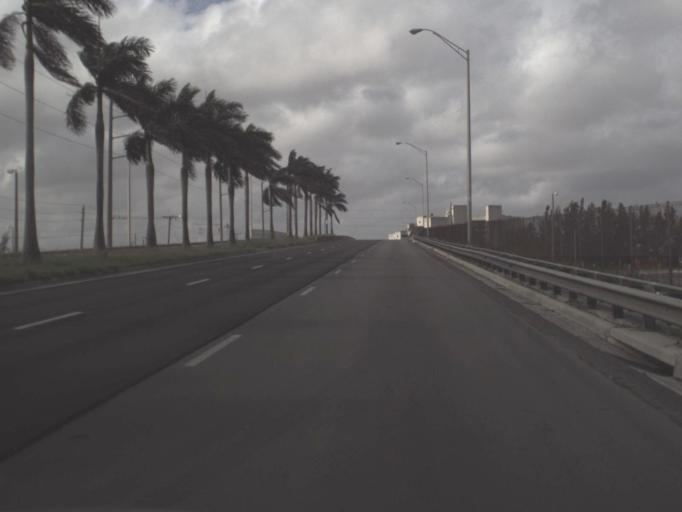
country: US
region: Florida
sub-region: Miami-Dade County
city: Virginia Gardens
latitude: 25.8079
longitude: -80.3059
